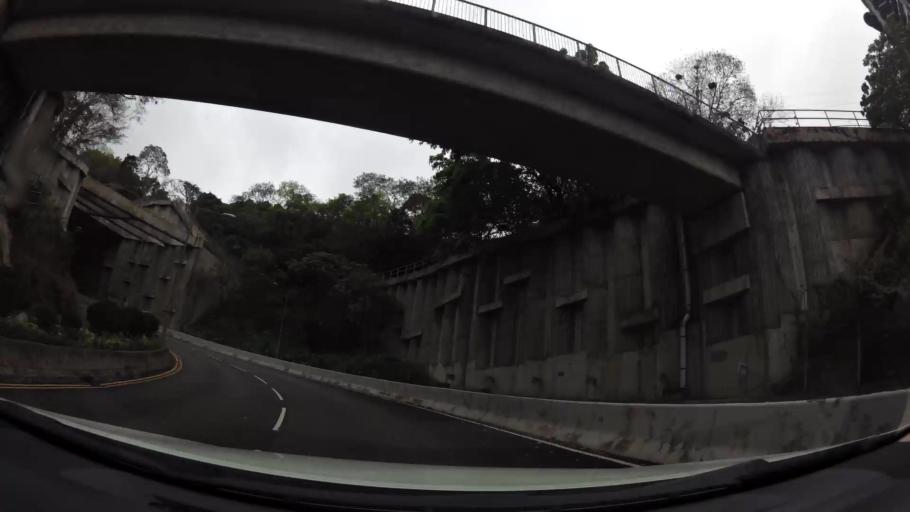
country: HK
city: Hong Kong
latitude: 22.2782
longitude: 114.1292
